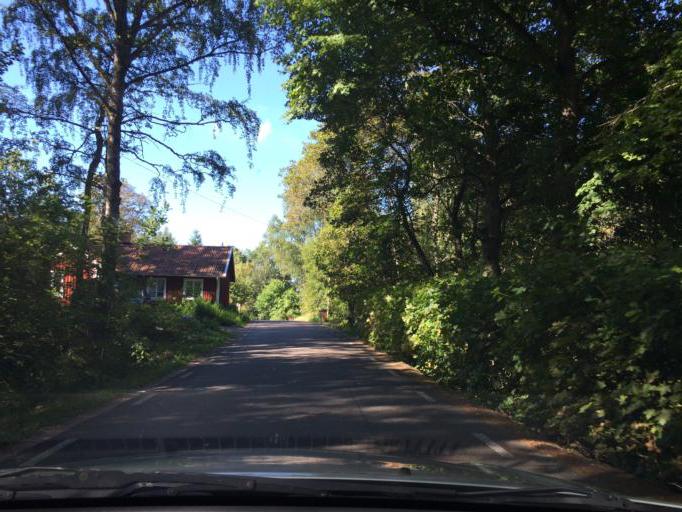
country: SE
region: Soedermanland
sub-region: Eskilstuna Kommun
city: Torshalla
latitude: 59.5080
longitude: 16.4147
